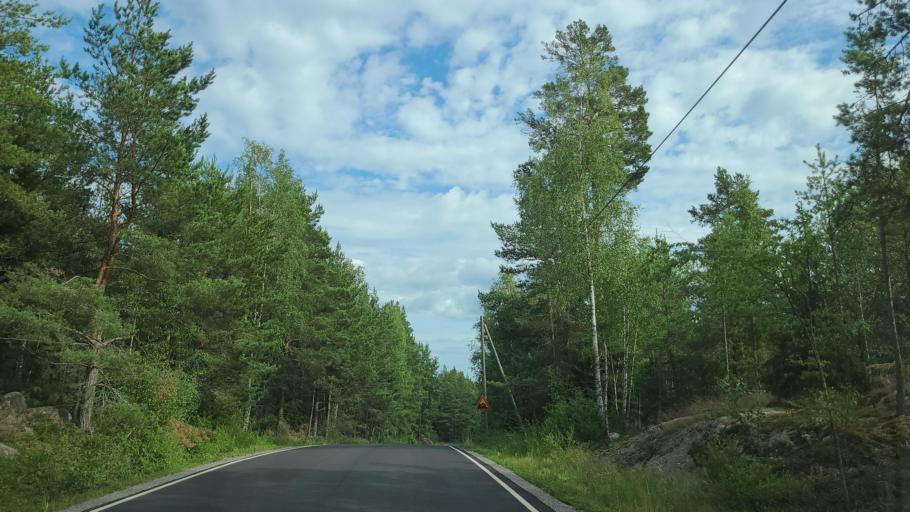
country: FI
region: Varsinais-Suomi
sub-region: Turku
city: Rymaettylae
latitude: 60.3195
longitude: 21.9600
